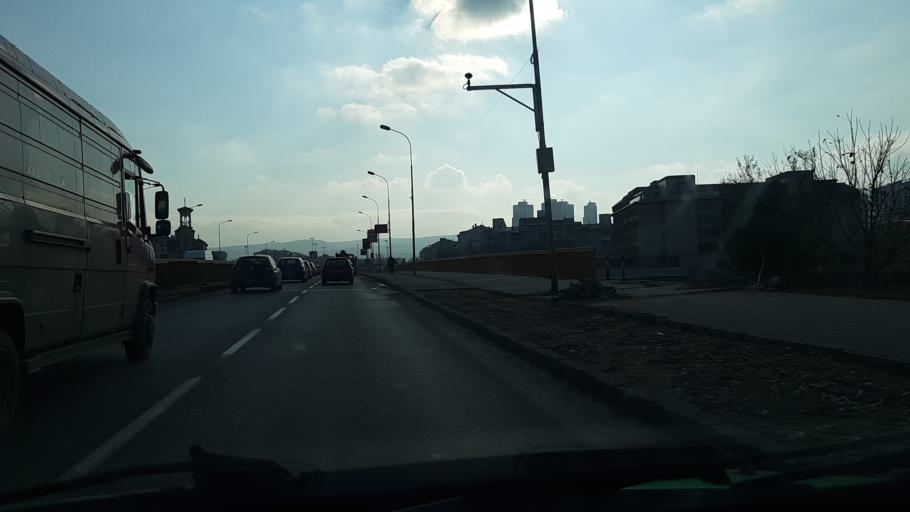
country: MK
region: Kisela Voda
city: Usje
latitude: 41.9919
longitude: 21.4747
